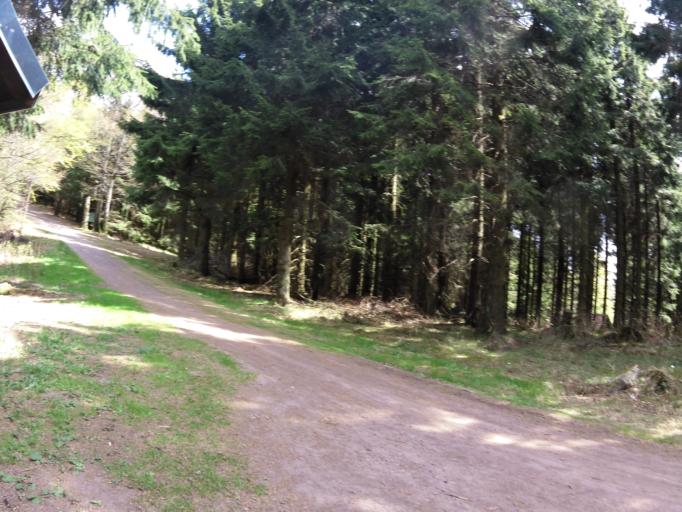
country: DE
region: Thuringia
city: Brotterode
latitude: 50.8459
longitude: 10.4552
